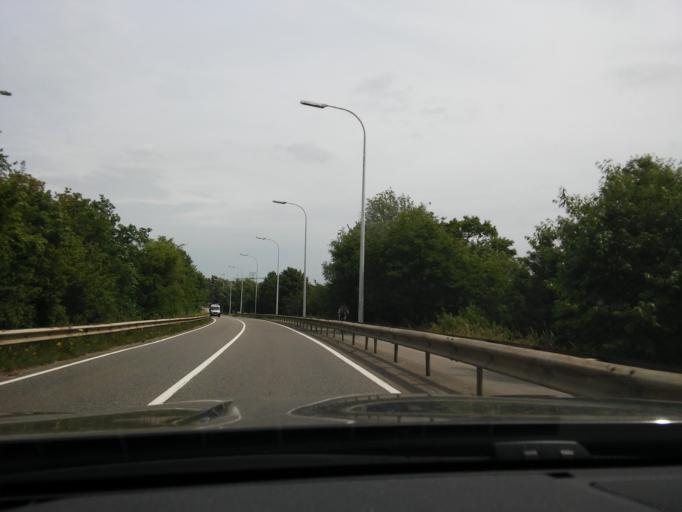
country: BE
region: Flanders
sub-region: Provincie Antwerpen
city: Rumst
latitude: 51.1044
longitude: 4.4356
